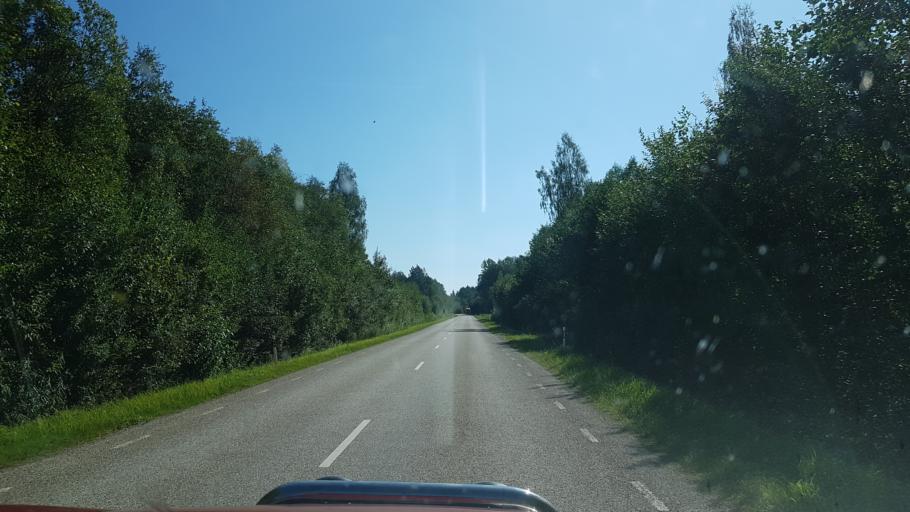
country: EE
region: Polvamaa
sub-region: Polva linn
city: Polva
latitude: 58.2495
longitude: 27.1854
